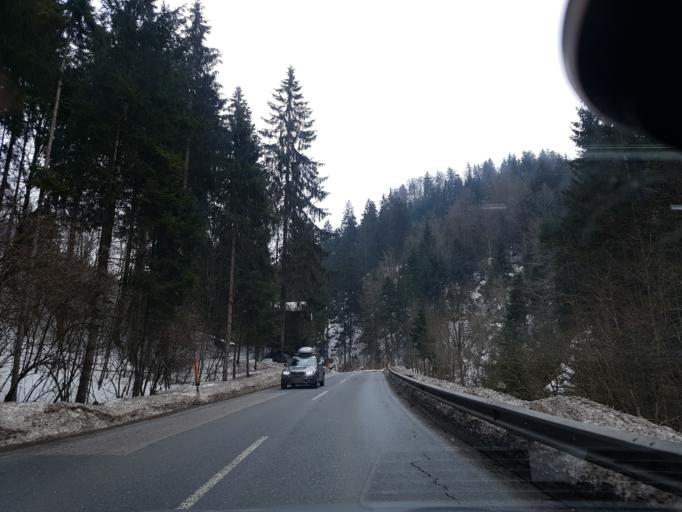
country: AT
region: Tyrol
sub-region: Politischer Bezirk Kufstein
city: Worgl
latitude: 47.4625
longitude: 12.0911
